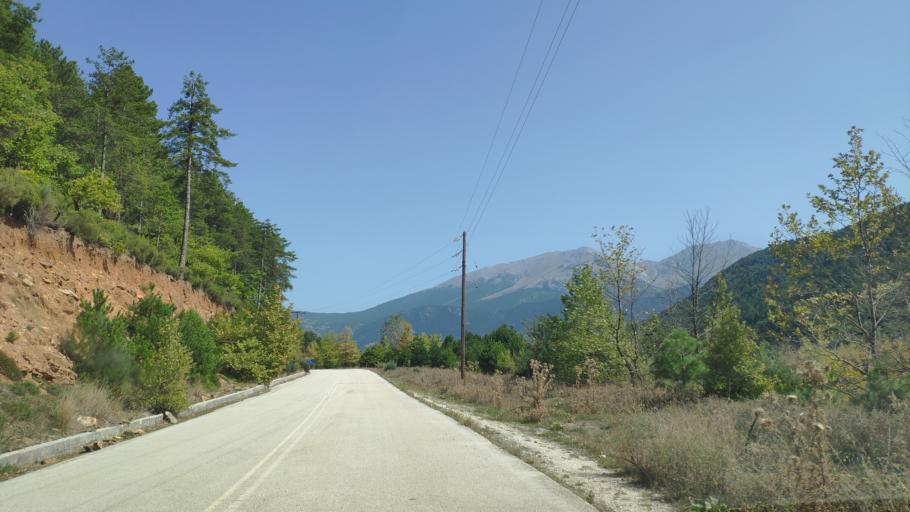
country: GR
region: West Greece
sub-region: Nomos Achaias
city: Kalavryta
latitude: 37.9314
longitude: 22.2865
